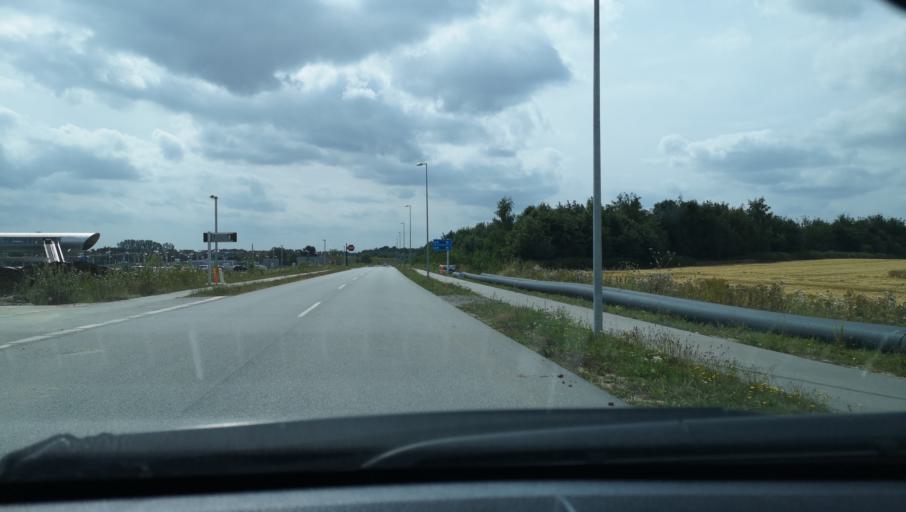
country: DK
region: Zealand
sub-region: Solrod Kommune
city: Solrod
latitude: 55.5017
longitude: 12.1713
